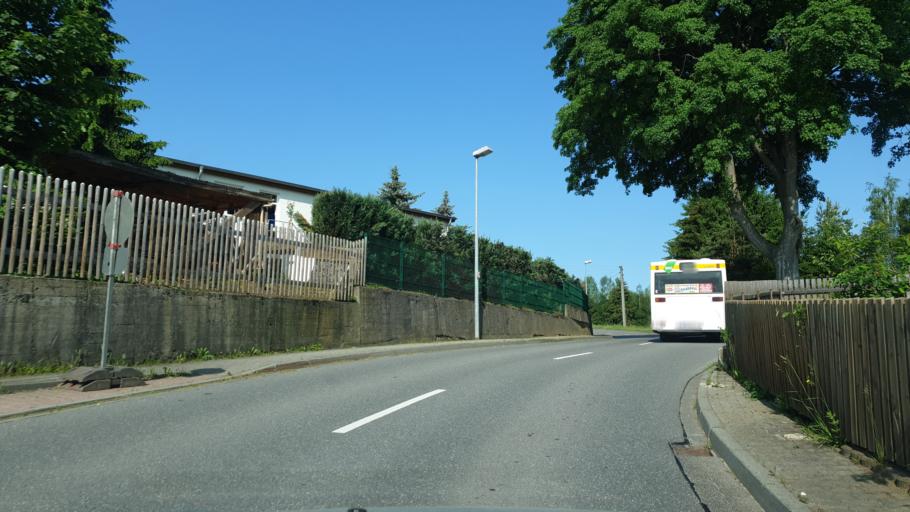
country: DE
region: Saxony
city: Zschorlau
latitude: 50.5598
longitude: 12.6359
